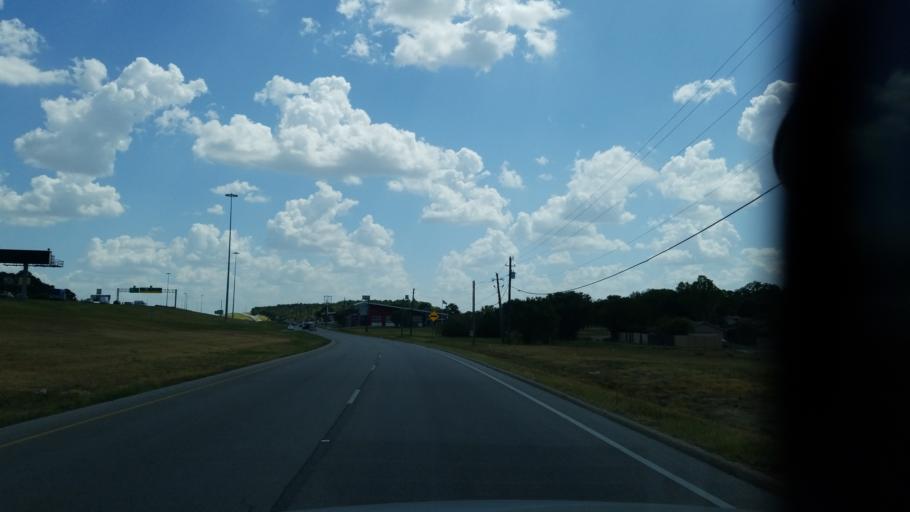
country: US
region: Texas
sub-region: Dallas County
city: Cockrell Hill
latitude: 32.7399
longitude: -96.9202
